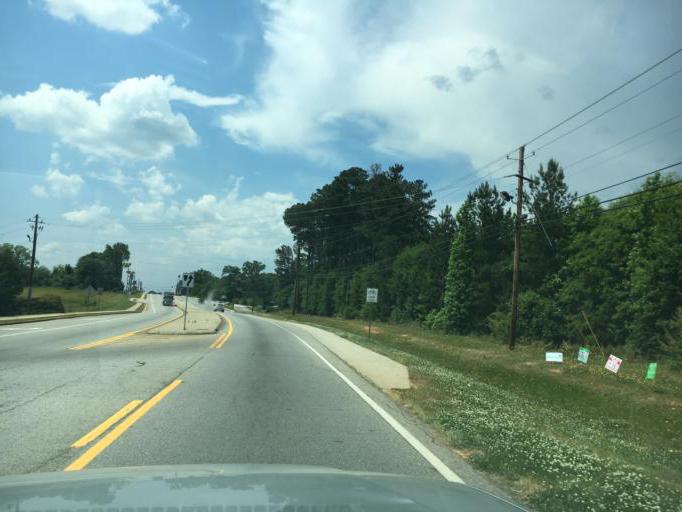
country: US
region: Georgia
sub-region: Franklin County
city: Lavonia
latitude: 34.4432
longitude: -83.1137
